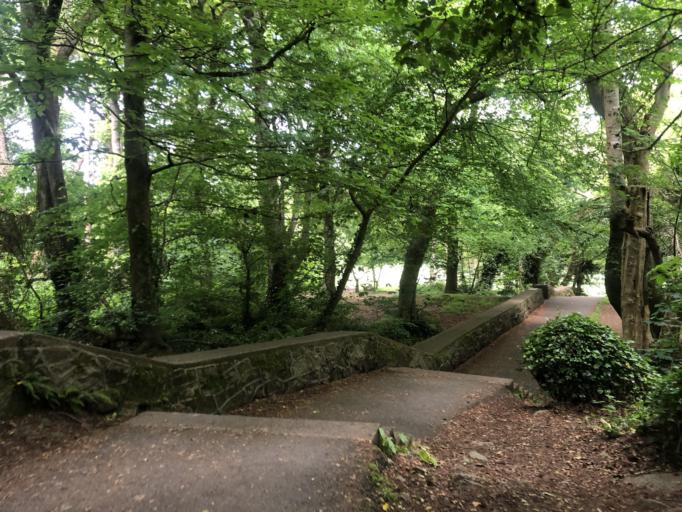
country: IE
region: Leinster
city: Dalkey
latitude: 53.2673
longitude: -6.1104
